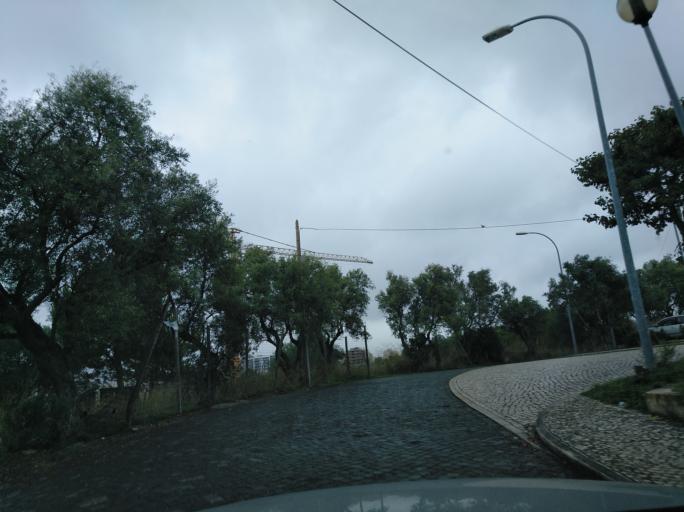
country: PT
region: Lisbon
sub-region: Loures
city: Sacavem
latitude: 38.7955
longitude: -9.1034
